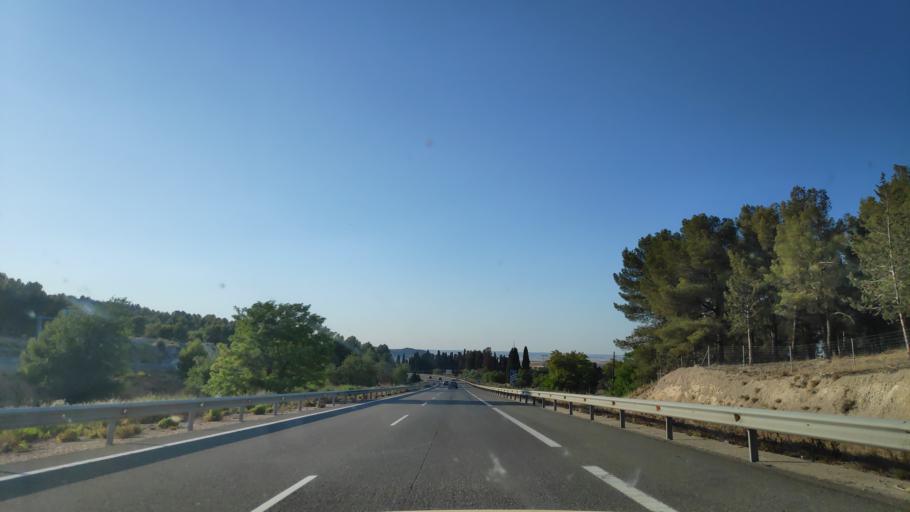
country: ES
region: Castille-La Mancha
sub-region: Provincia de Cuenca
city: Belinchon
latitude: 40.0251
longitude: -3.0355
